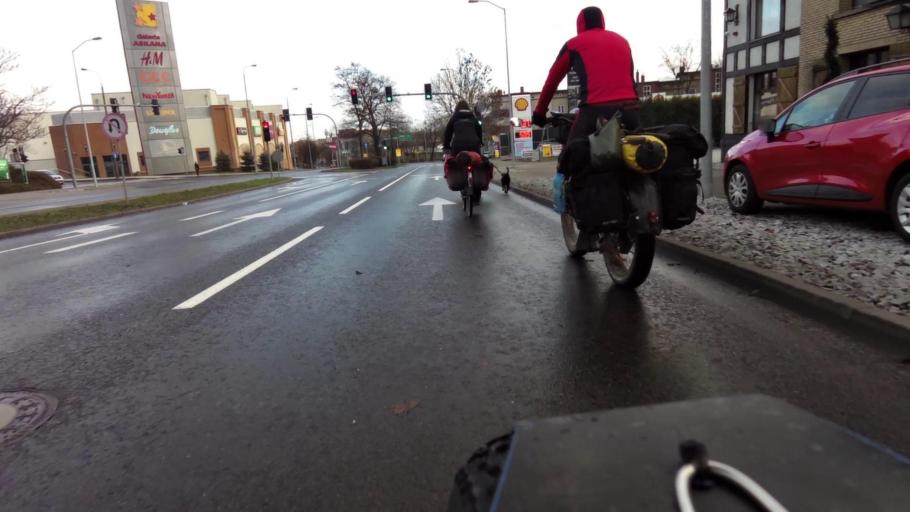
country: PL
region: Lubusz
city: Gorzow Wielkopolski
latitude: 52.7311
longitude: 15.2229
